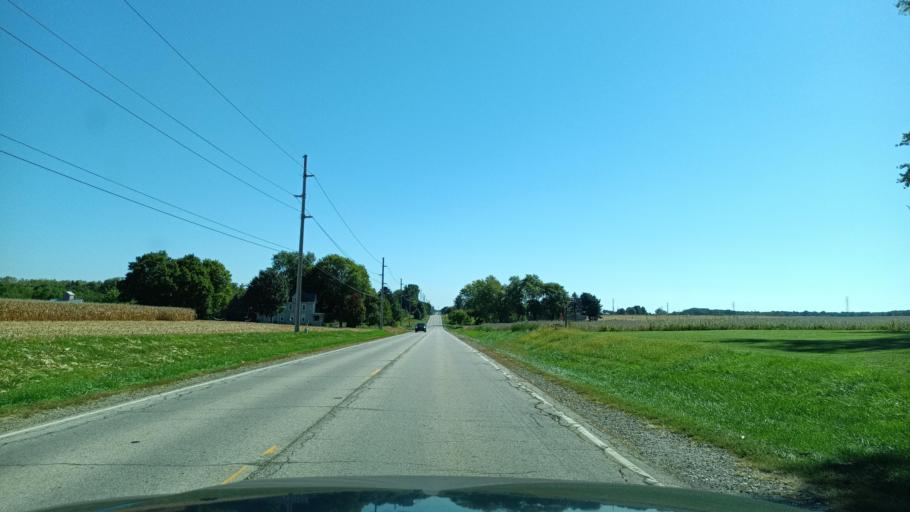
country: US
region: Illinois
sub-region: Peoria County
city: Dunlap
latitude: 40.7849
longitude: -89.7212
